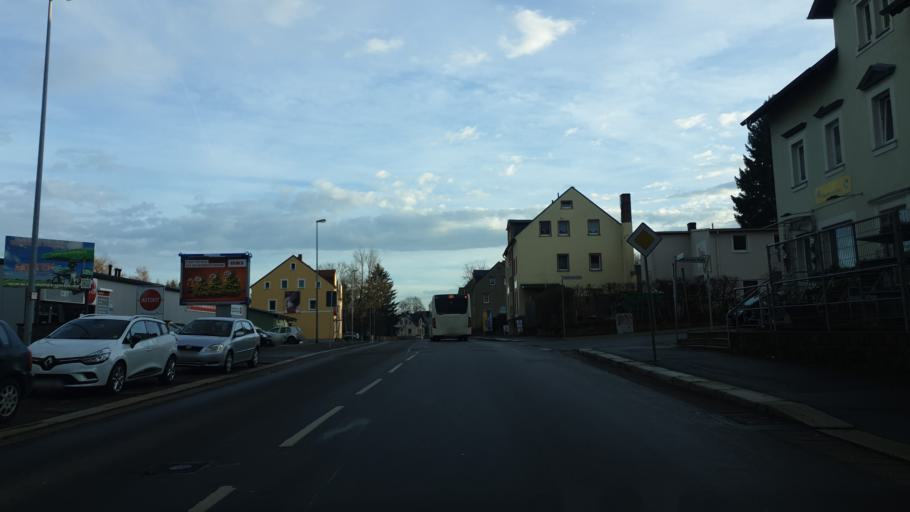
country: DE
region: Saxony
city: Neukirchen
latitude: 50.8125
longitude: 12.8302
